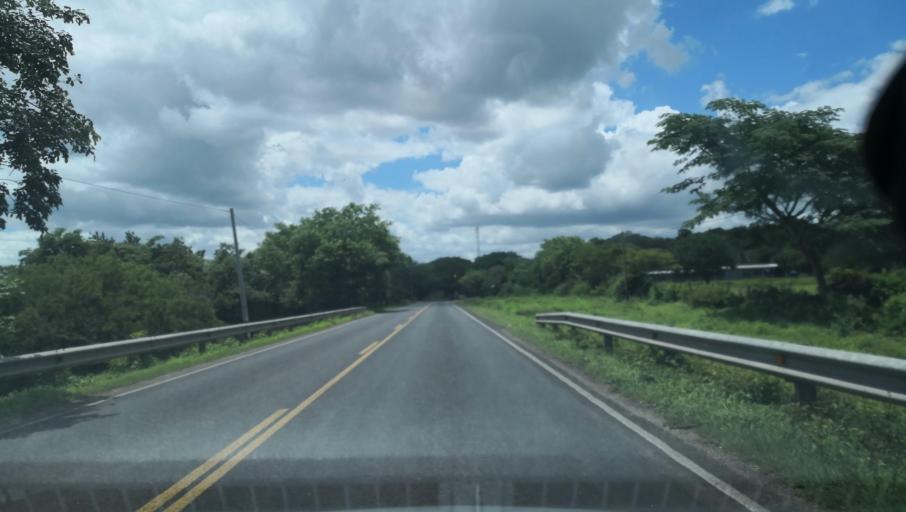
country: NI
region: Esteli
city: Condega
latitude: 13.4044
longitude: -86.4000
